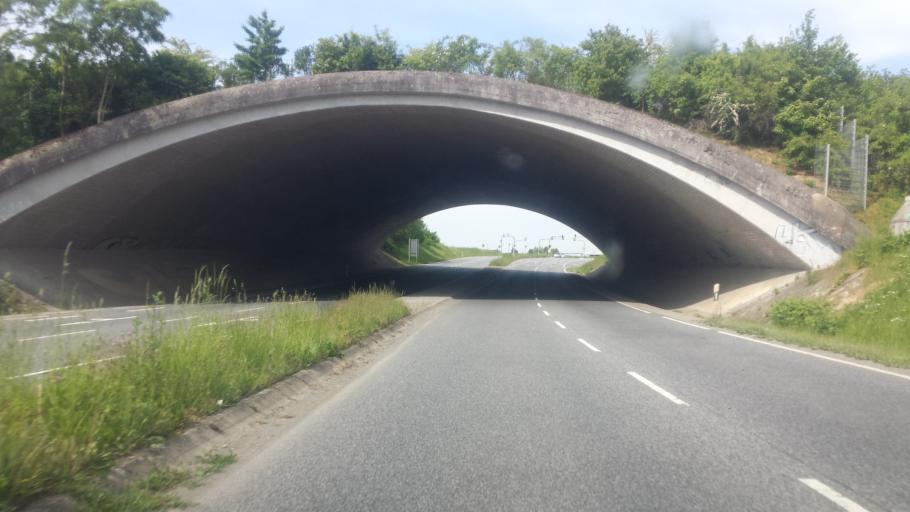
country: DE
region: Hesse
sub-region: Regierungsbezirk Darmstadt
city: Bad Vilbel
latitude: 50.1935
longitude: 8.7385
